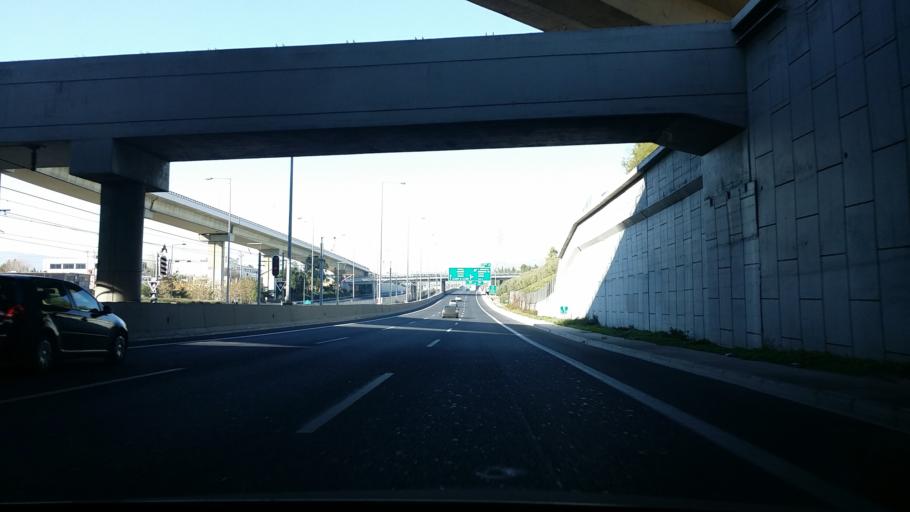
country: GR
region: Attica
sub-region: Nomarchia Athinas
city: Metamorfosi
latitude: 38.0621
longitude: 23.7497
